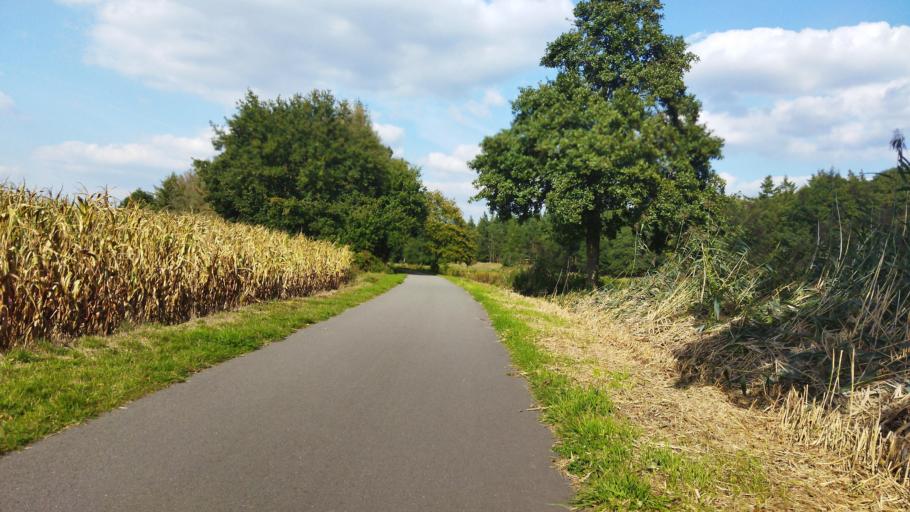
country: DE
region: Lower Saxony
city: Walchum
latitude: 52.9388
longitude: 7.2925
